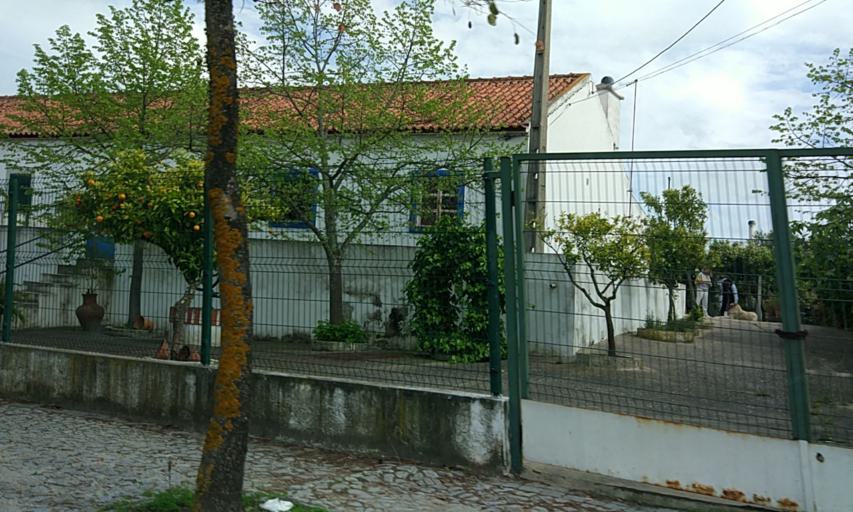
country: PT
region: Evora
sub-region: Evora
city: Evora
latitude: 38.5674
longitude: -7.9296
